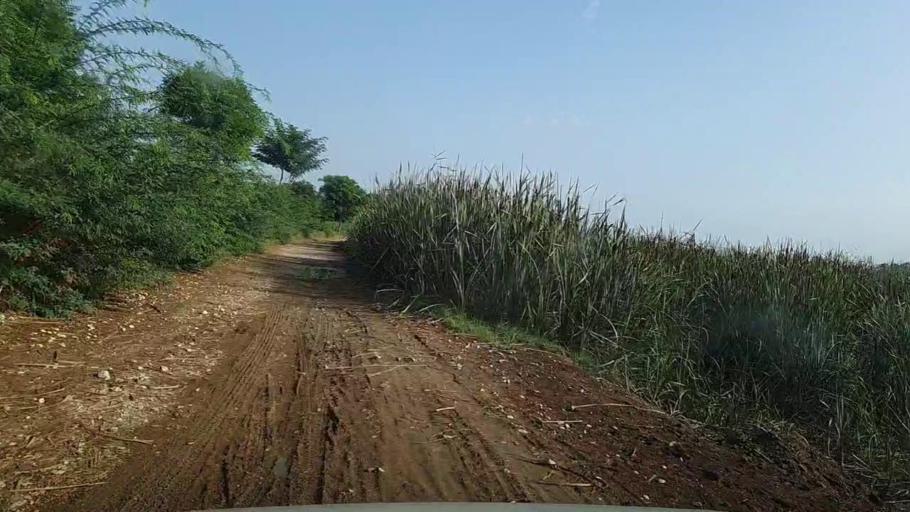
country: PK
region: Sindh
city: Pad Idan
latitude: 26.8347
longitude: 68.2411
